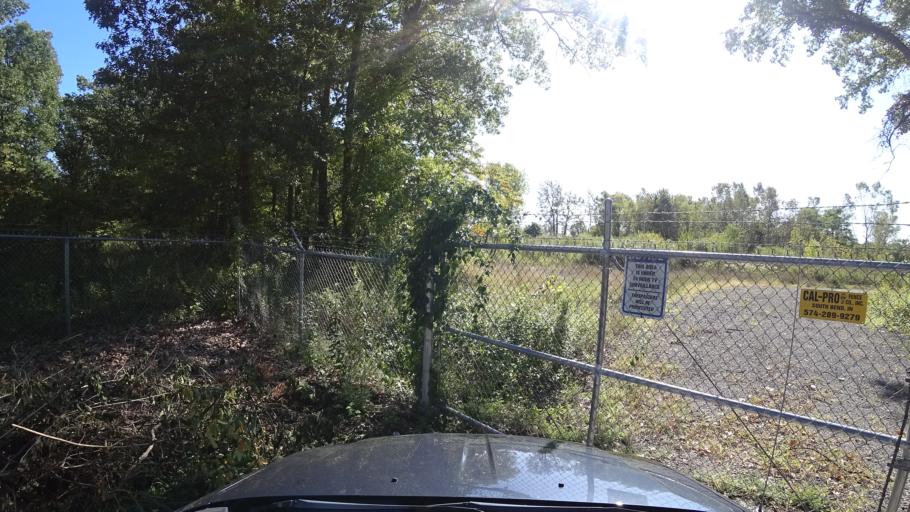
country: US
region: Indiana
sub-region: LaPorte County
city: Michigan City
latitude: 41.7260
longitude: -86.8844
